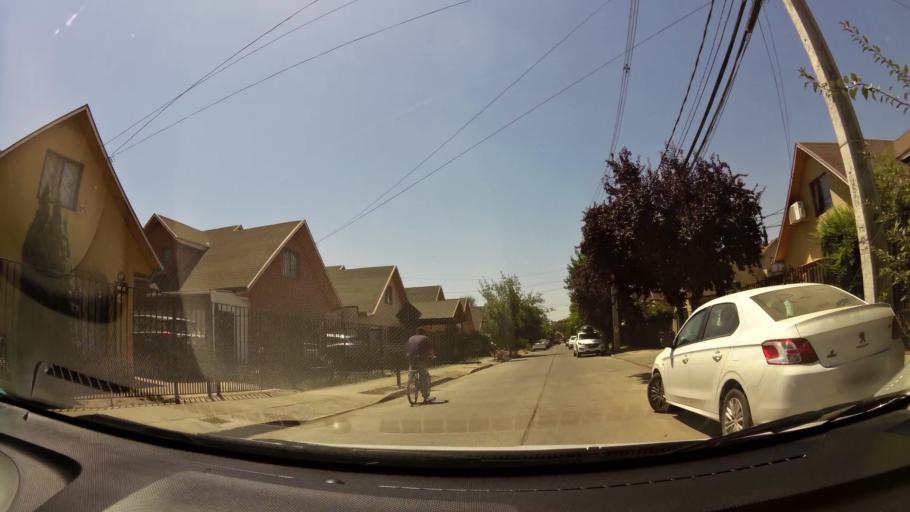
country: CL
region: Maule
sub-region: Provincia de Talca
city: Talca
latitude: -35.4266
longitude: -71.6208
